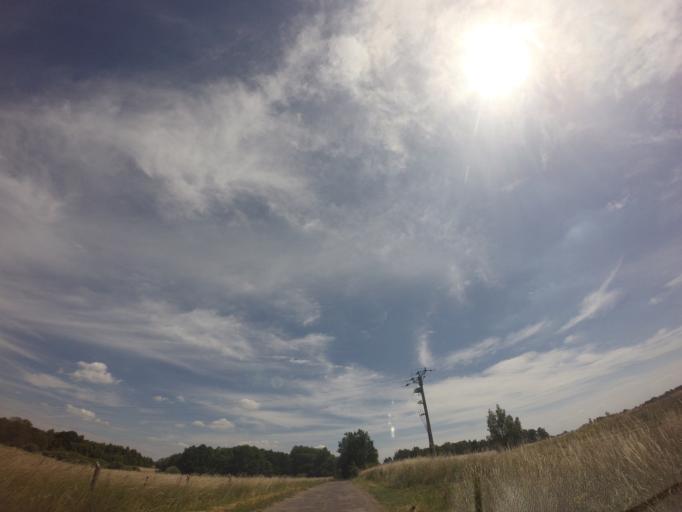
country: PL
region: West Pomeranian Voivodeship
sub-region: Powiat choszczenski
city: Recz
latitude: 53.3388
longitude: 15.5607
